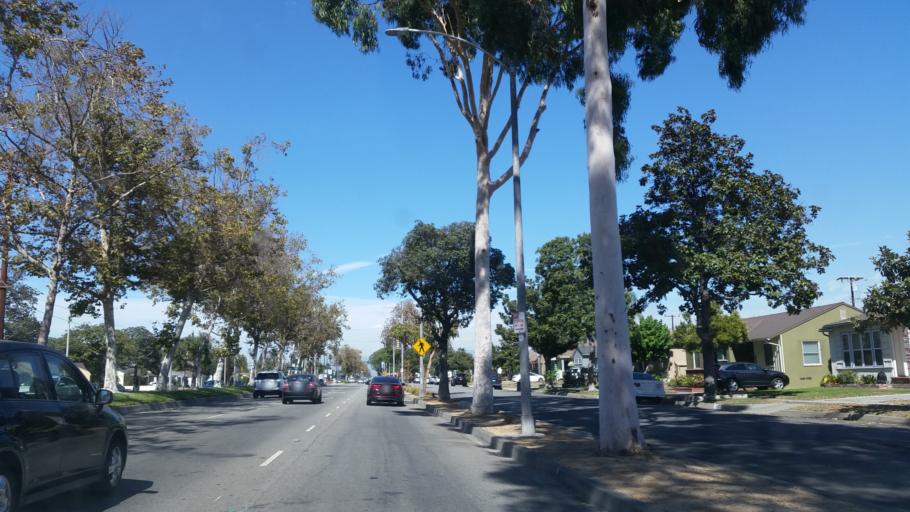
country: US
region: California
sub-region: Los Angeles County
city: Lakewood
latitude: 33.8552
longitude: -118.1424
